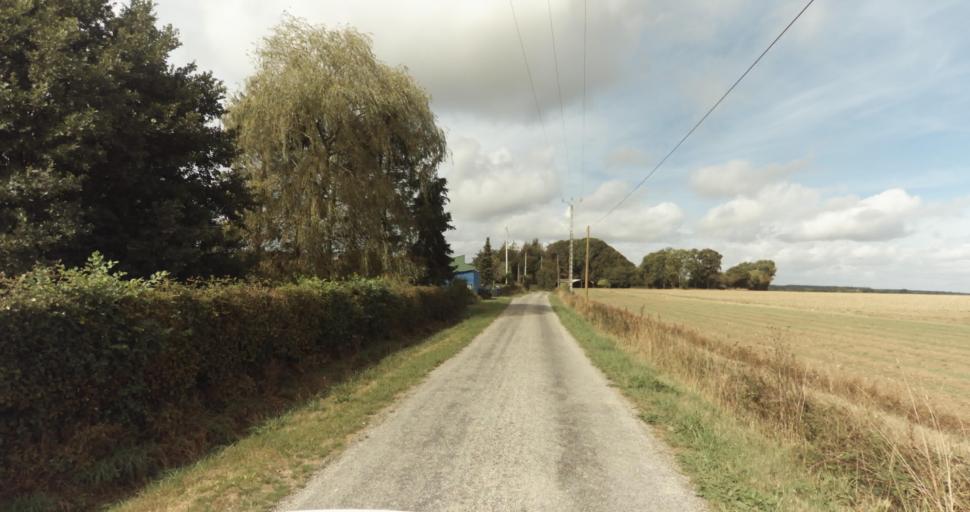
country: FR
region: Lower Normandy
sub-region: Departement de l'Orne
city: Gace
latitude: 48.8115
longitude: 0.3819
